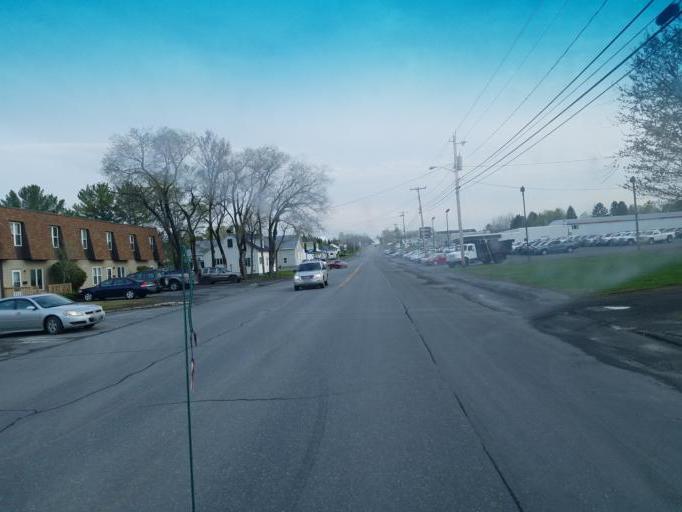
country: US
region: Maine
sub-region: Aroostook County
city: Caribou
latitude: 46.8477
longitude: -68.0108
